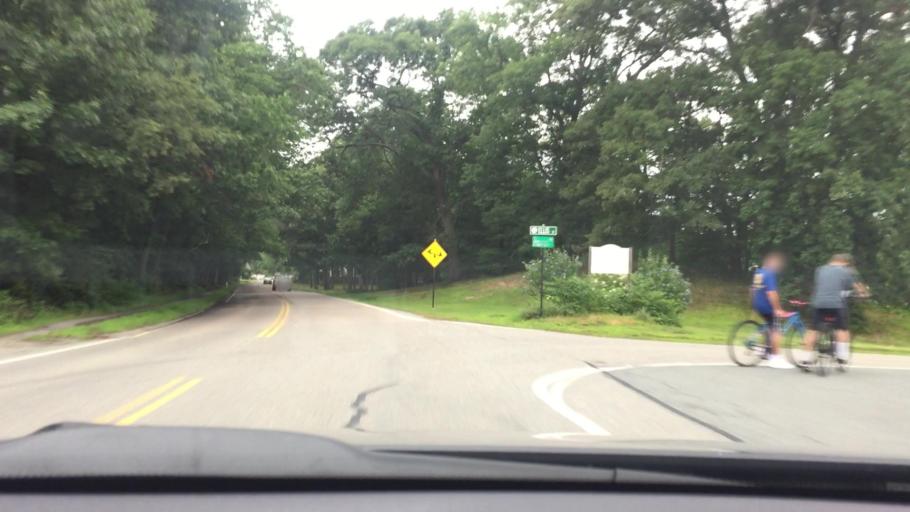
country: US
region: Massachusetts
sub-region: Norfolk County
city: Needham
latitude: 42.3065
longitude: -71.2303
